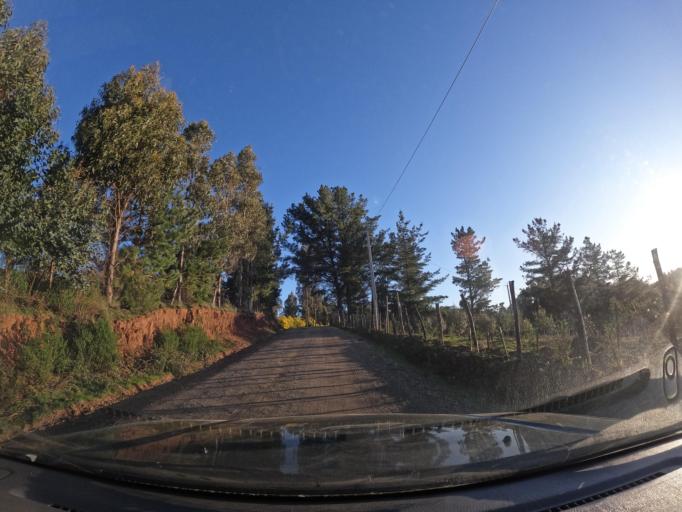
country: CL
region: Biobio
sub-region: Provincia de Concepcion
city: Chiguayante
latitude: -37.0151
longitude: -72.8490
